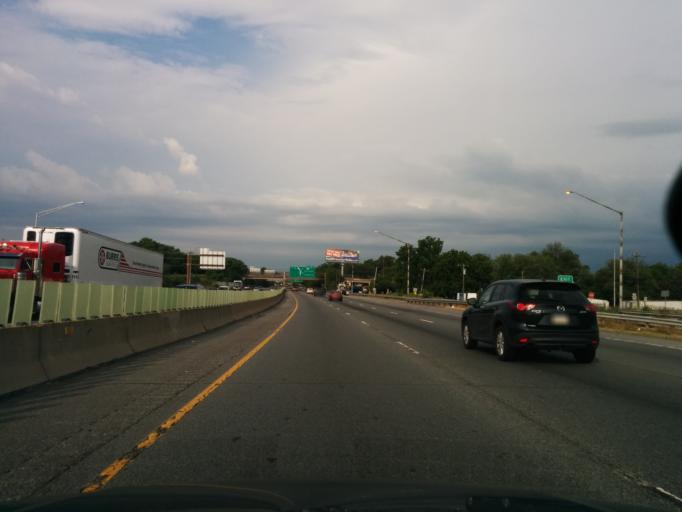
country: US
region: Pennsylvania
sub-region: Delaware County
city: Upland
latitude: 39.8460
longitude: -75.3907
